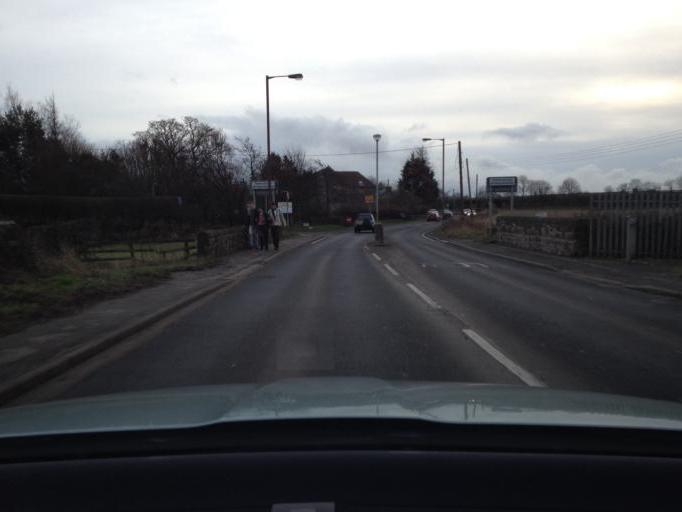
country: GB
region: Scotland
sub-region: Edinburgh
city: Kirkliston
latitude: 55.9503
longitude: -3.4057
